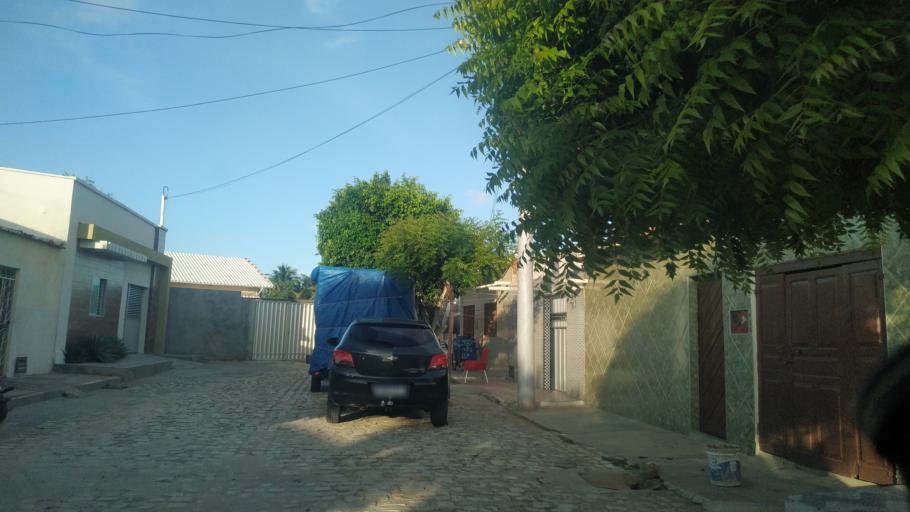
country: BR
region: Rio Grande do Norte
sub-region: Areia Branca
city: Areia Branca
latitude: -4.9510
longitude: -37.1282
